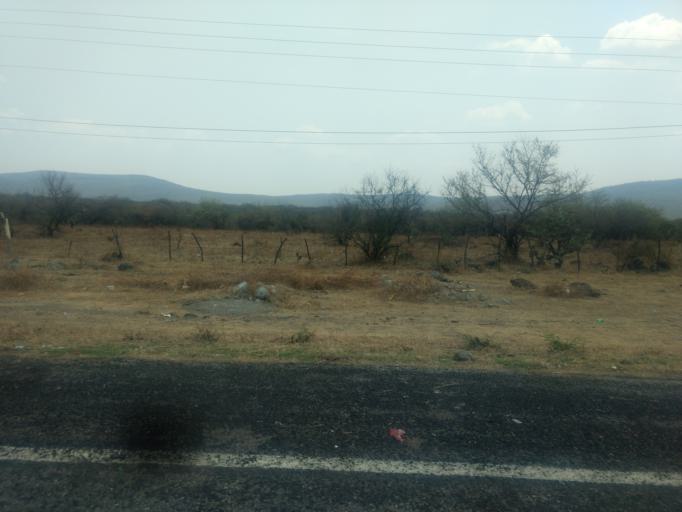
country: MX
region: Morelos
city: La Joya
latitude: 18.6743
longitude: -99.4352
